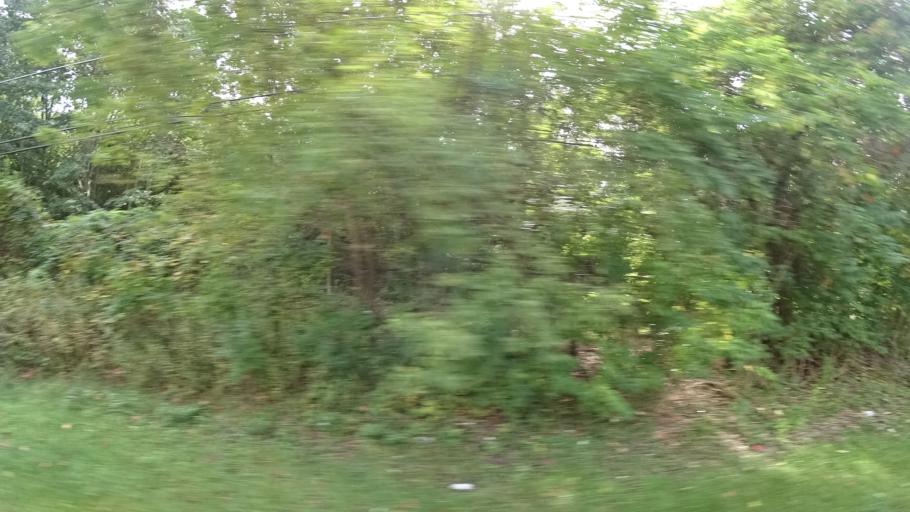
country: US
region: Indiana
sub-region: LaPorte County
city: Trail Creek
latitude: 41.7092
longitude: -86.8480
